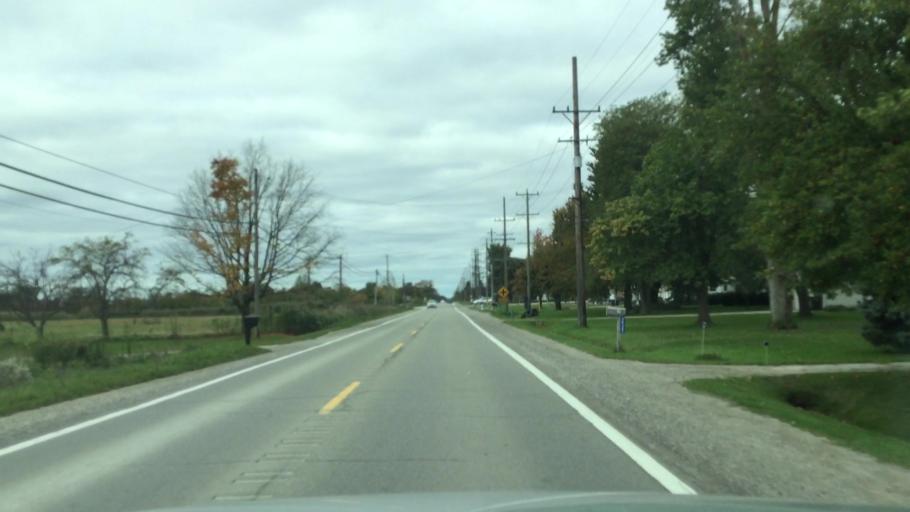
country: US
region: Michigan
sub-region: Macomb County
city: Richmond
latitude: 42.8089
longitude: -82.7715
